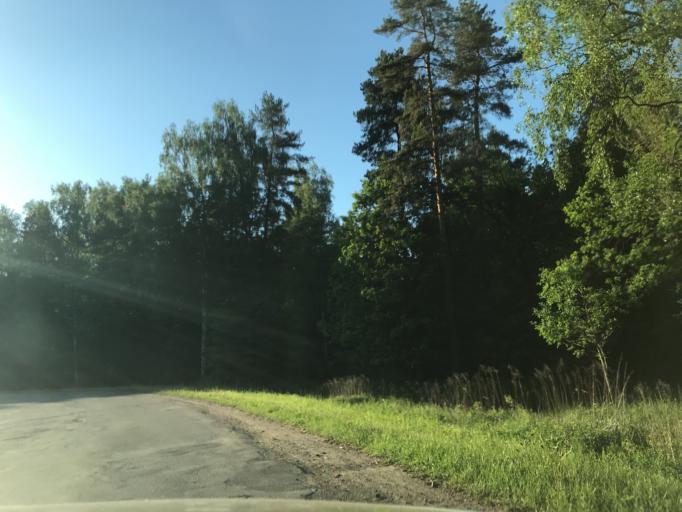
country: LV
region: Jelgava
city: Jelgava
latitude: 56.6256
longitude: 23.7648
